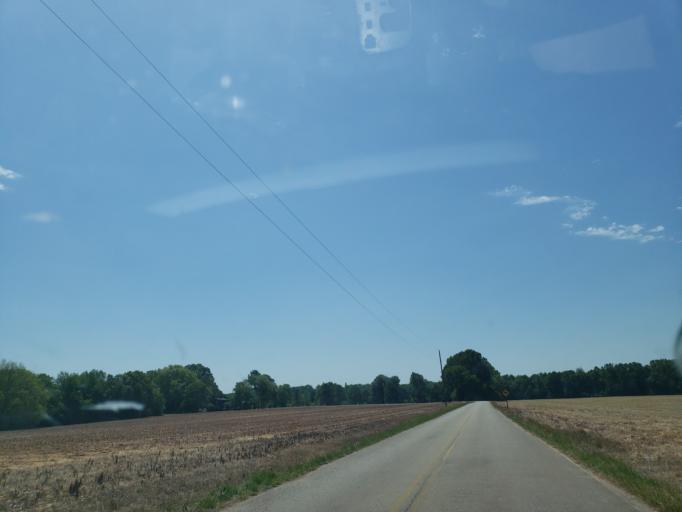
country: US
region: Alabama
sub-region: Madison County
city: Hazel Green
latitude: 34.9459
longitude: -86.5355
